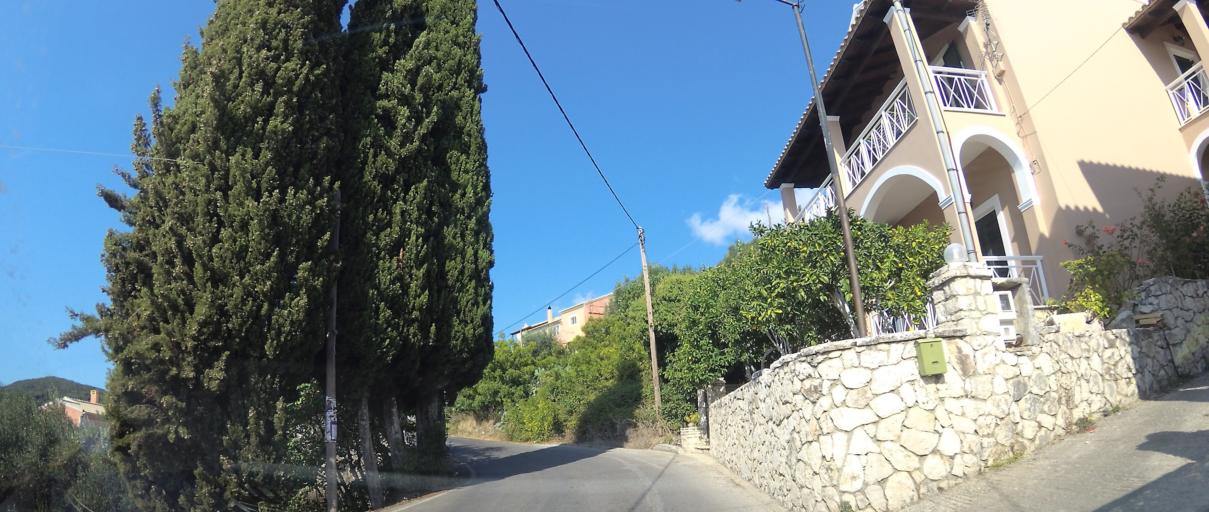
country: GR
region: Ionian Islands
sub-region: Nomos Kerkyras
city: Kontokali
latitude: 39.7194
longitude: 19.8455
